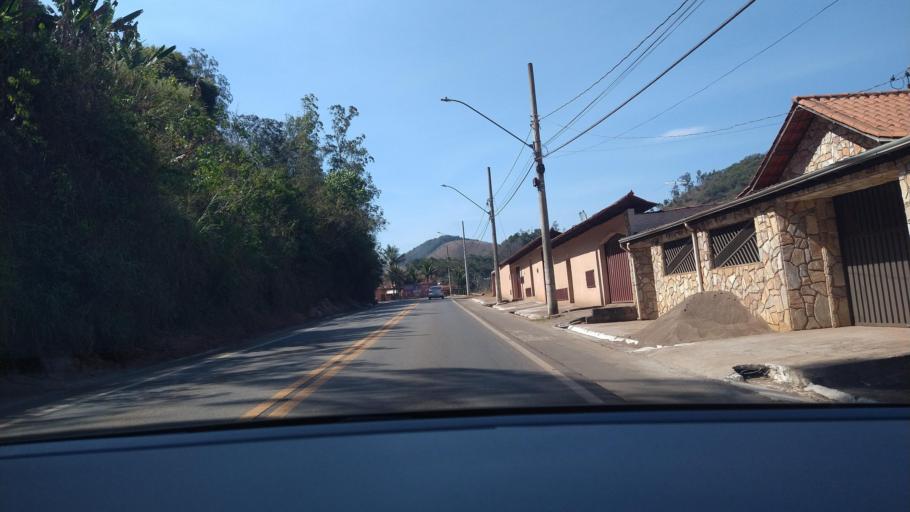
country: BR
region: Minas Gerais
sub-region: Rio Piracicaba
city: Rio Piracicaba
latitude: -19.9262
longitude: -43.1658
